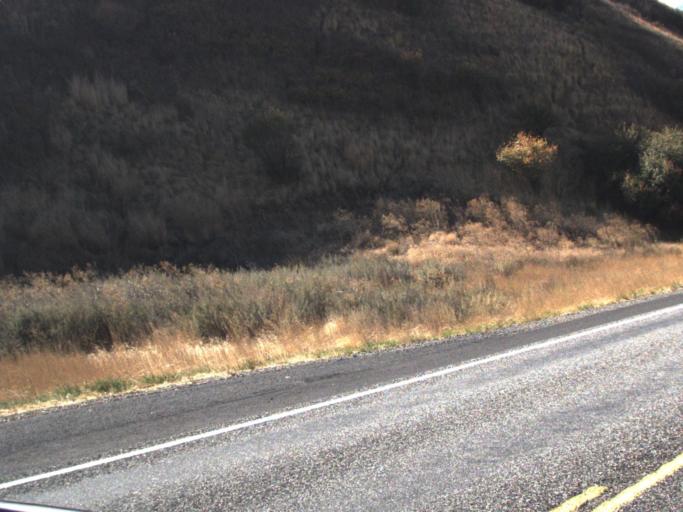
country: US
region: Washington
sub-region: Walla Walla County
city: Waitsburg
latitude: 46.2688
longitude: -118.1806
